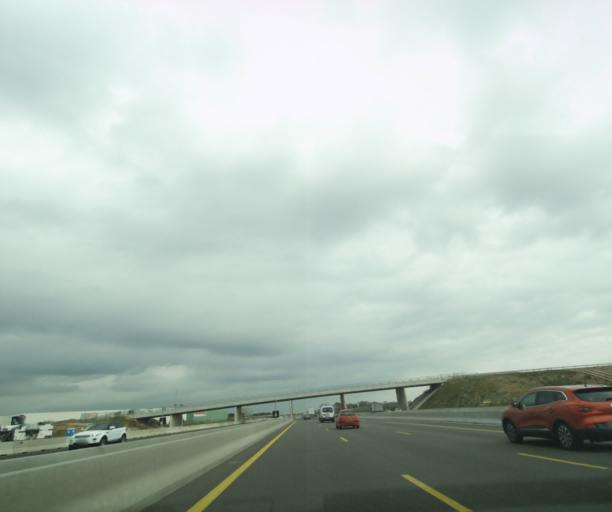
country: FR
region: Languedoc-Roussillon
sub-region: Departement de l'Herault
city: Vendargues
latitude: 43.6483
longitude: 3.9827
